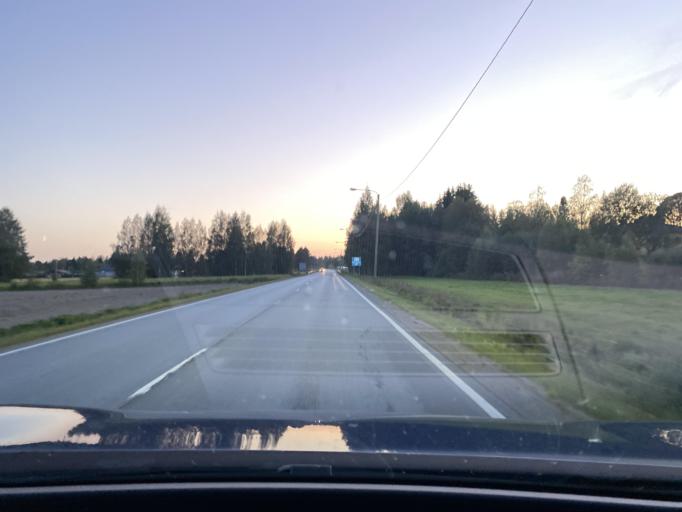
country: FI
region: Southern Ostrobothnia
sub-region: Seinaejoki
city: Kauhava
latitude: 63.1073
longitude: 23.0513
